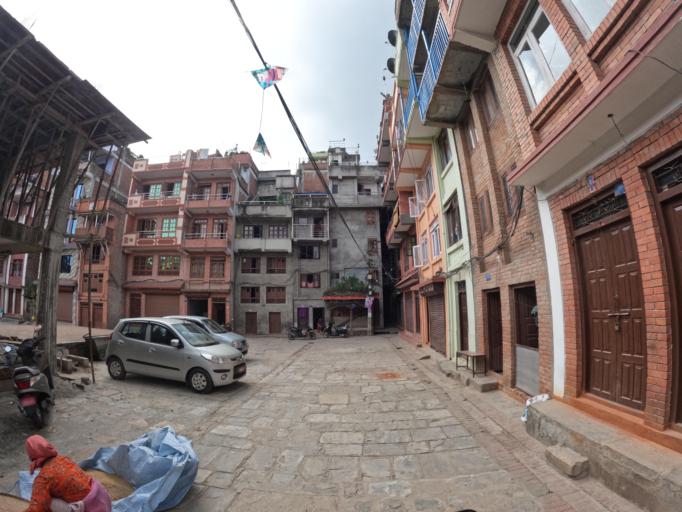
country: NP
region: Central Region
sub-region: Bagmati Zone
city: Bhaktapur
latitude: 27.6805
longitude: 85.3869
